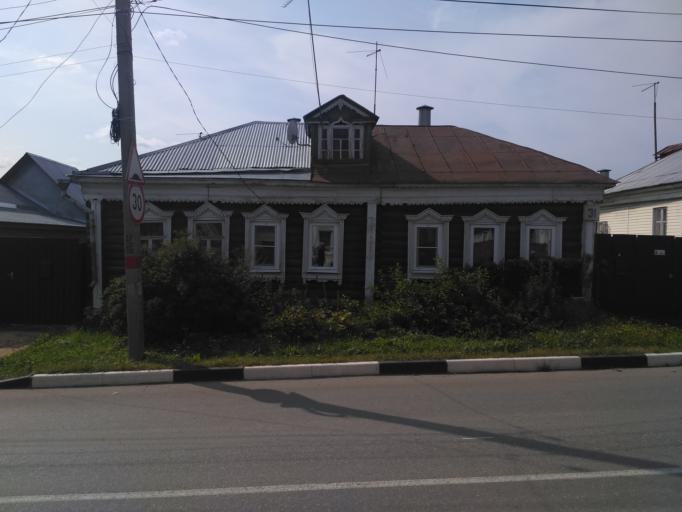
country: RU
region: Moskovskaya
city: Sergiyev Posad
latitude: 56.3164
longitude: 38.1242
